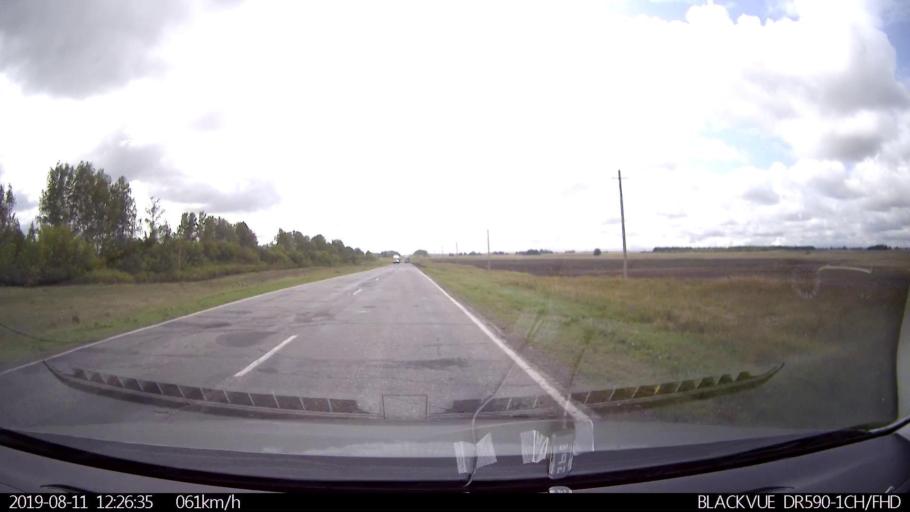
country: RU
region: Ulyanovsk
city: Ignatovka
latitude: 53.8627
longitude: 47.9292
